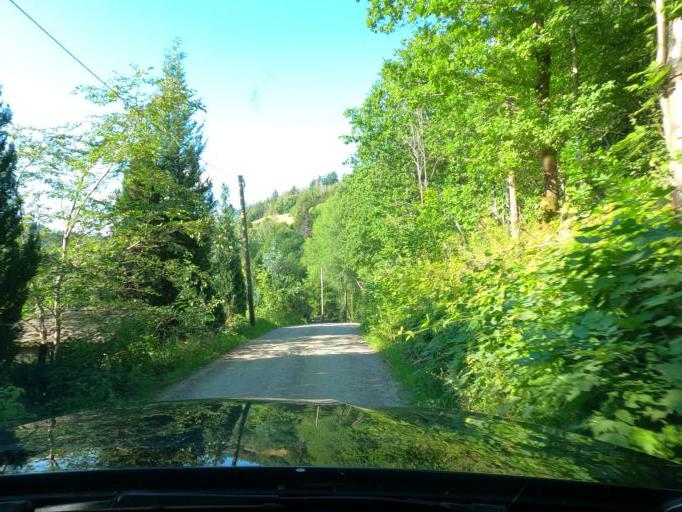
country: DE
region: Lower Saxony
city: Osterode am Harz
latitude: 51.7465
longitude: 10.2924
